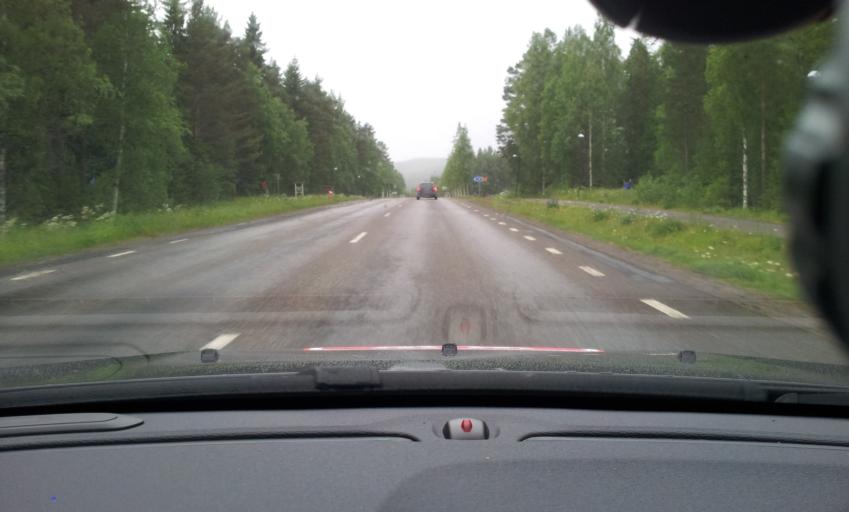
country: SE
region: Jaemtland
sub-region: Ragunda Kommun
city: Hammarstrand
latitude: 63.0172
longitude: 16.6494
